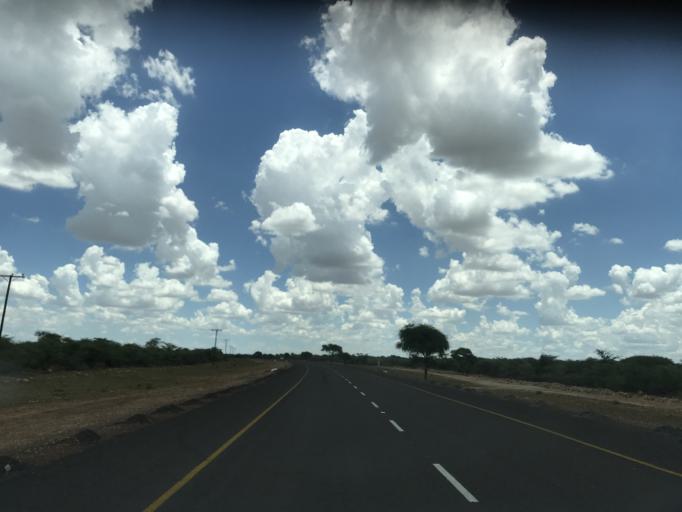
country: BW
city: Mabuli
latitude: -25.8060
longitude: 24.7657
